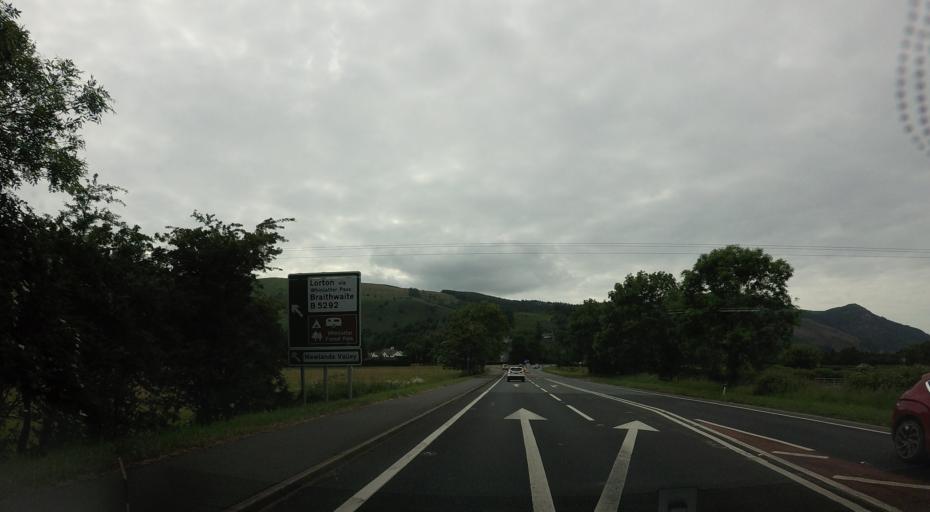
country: GB
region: England
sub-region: Cumbria
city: Keswick
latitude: 54.6018
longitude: -3.1813
